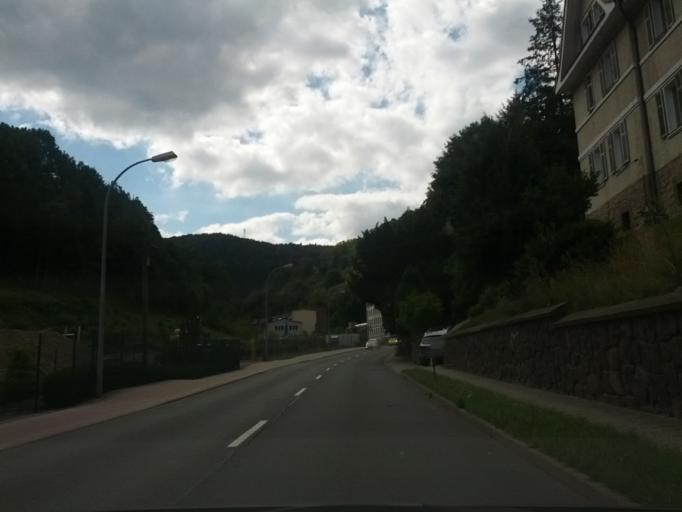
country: DE
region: Thuringia
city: Ruhla
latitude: 50.9038
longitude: 10.3698
